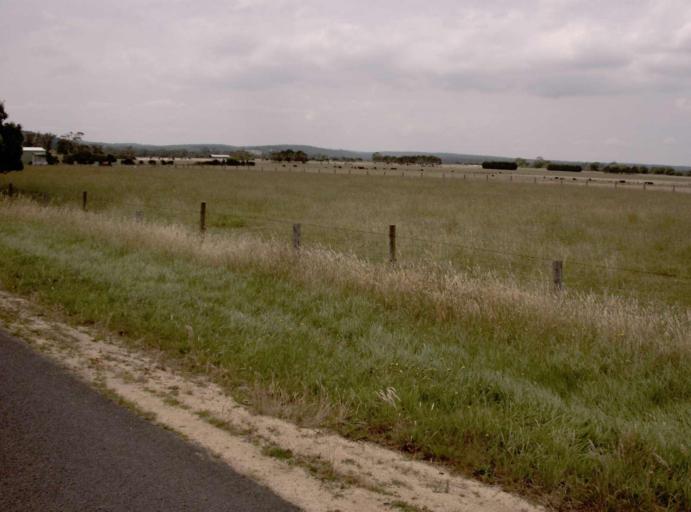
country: AU
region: Victoria
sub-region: Latrobe
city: Traralgon
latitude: -38.4948
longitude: 146.6790
